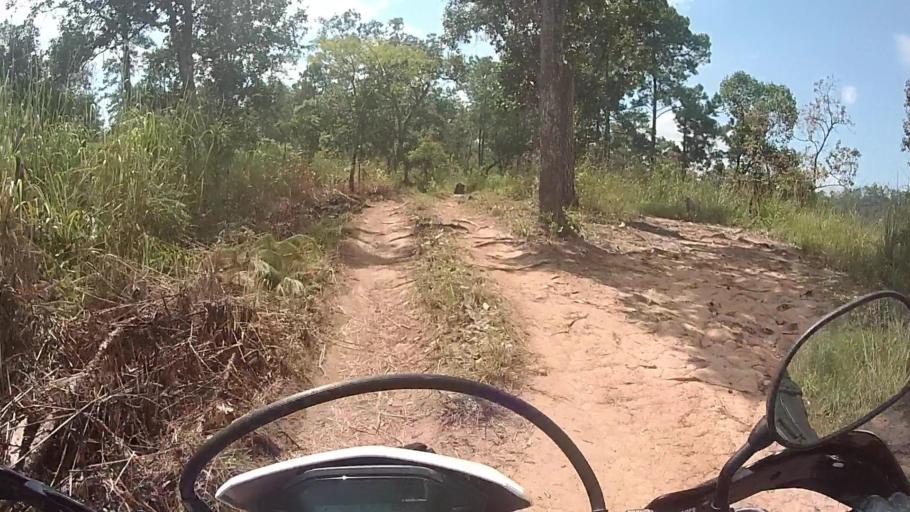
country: TH
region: Chiang Mai
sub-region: Amphoe Chiang Dao
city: Chiang Dao
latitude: 19.3191
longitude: 98.7950
